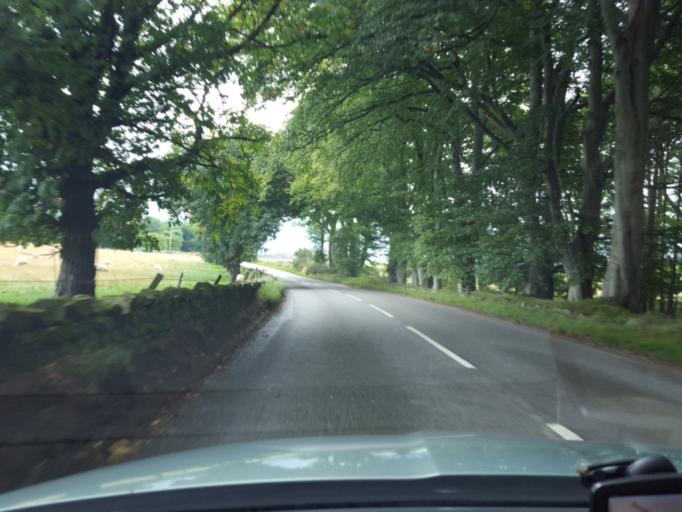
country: GB
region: Scotland
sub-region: Aberdeenshire
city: Kemnay
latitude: 57.1687
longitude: -2.4204
